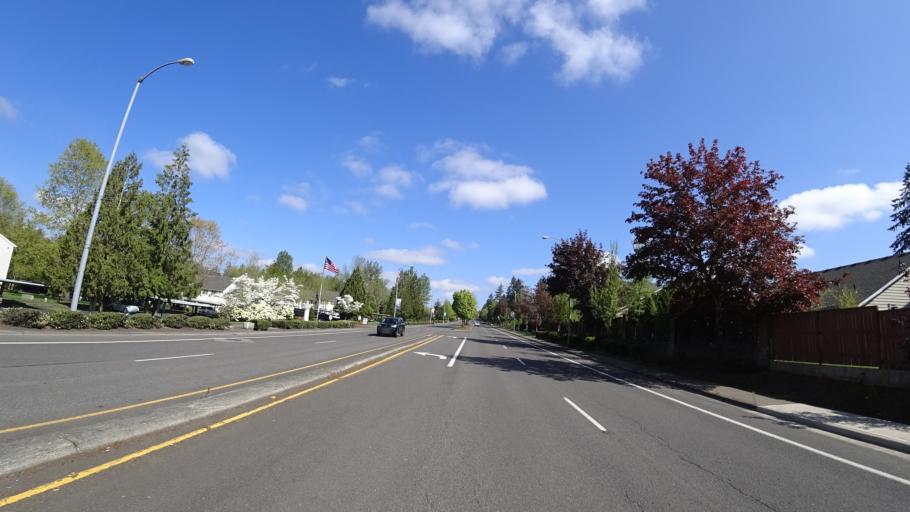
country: US
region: Oregon
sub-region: Washington County
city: Beaverton
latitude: 45.4452
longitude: -122.8260
